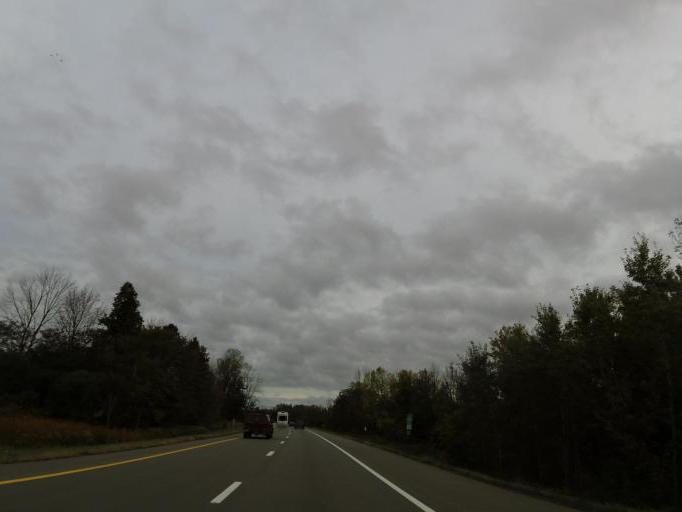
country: US
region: New York
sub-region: Erie County
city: Elma Center
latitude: 42.8266
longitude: -78.6721
